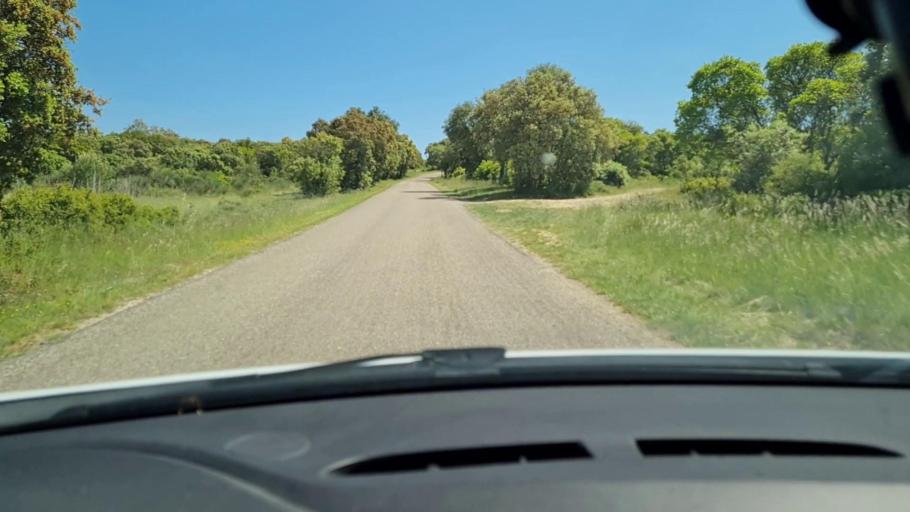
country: FR
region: Languedoc-Roussillon
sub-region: Departement du Gard
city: Clarensac
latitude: 43.8460
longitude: 4.1905
